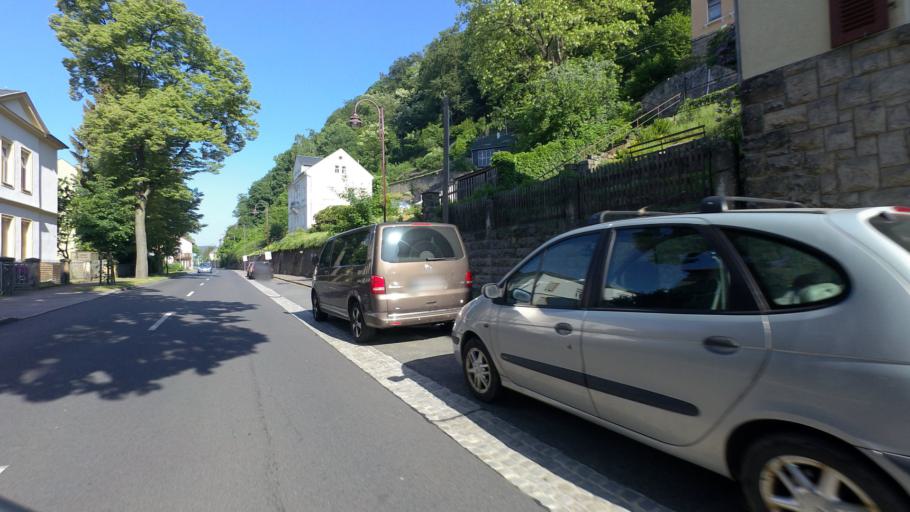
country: DE
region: Saxony
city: Bad Schandau
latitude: 50.9203
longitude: 14.1479
